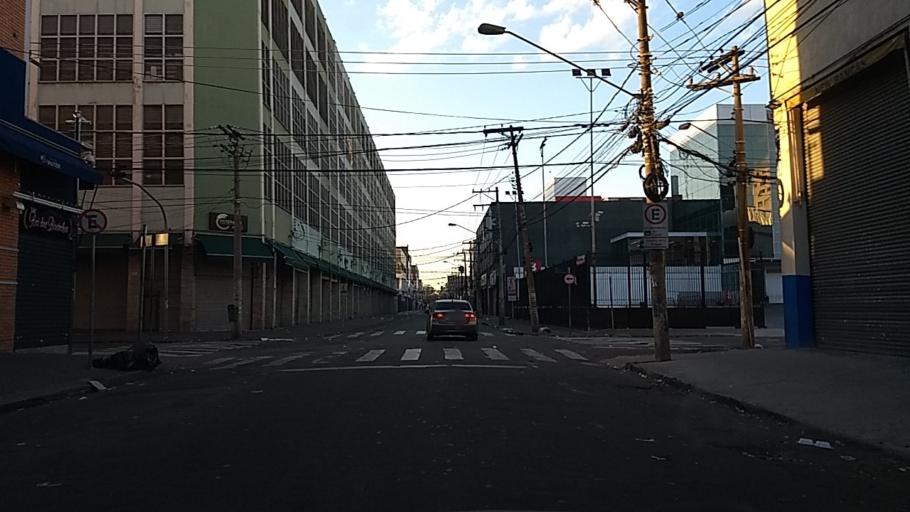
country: BR
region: Sao Paulo
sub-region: Sao Paulo
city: Sao Paulo
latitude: -23.5332
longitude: -46.6208
